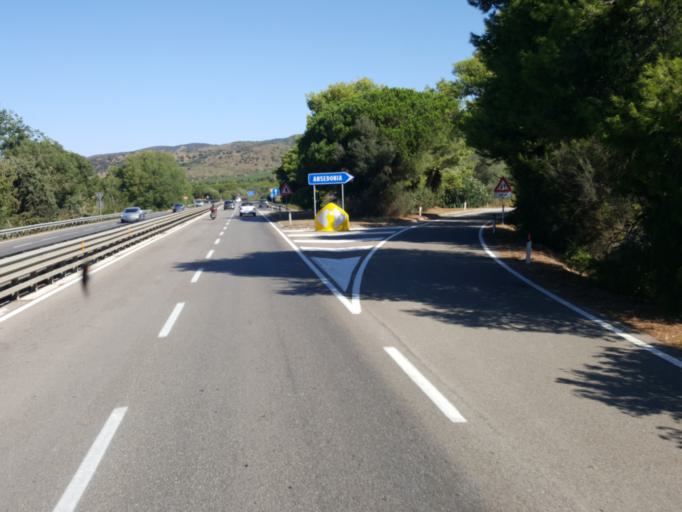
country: IT
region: Tuscany
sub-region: Provincia di Grosseto
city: Orbetello Scalo
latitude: 42.4278
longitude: 11.2866
